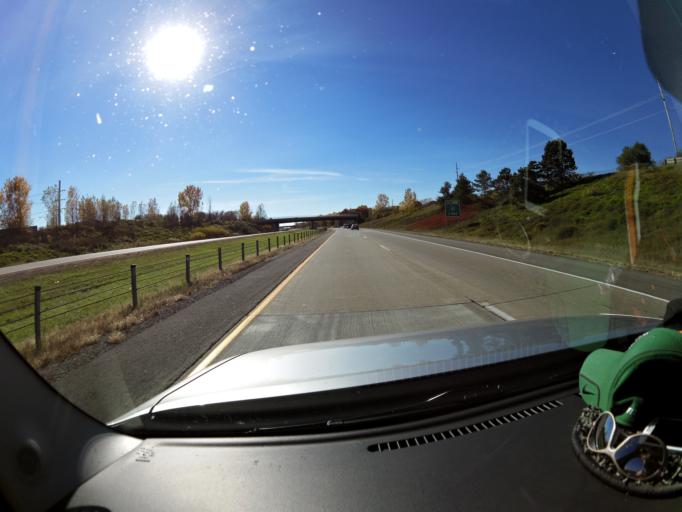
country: US
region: Minnesota
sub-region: Dakota County
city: Burnsville
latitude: 44.7553
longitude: -93.2579
